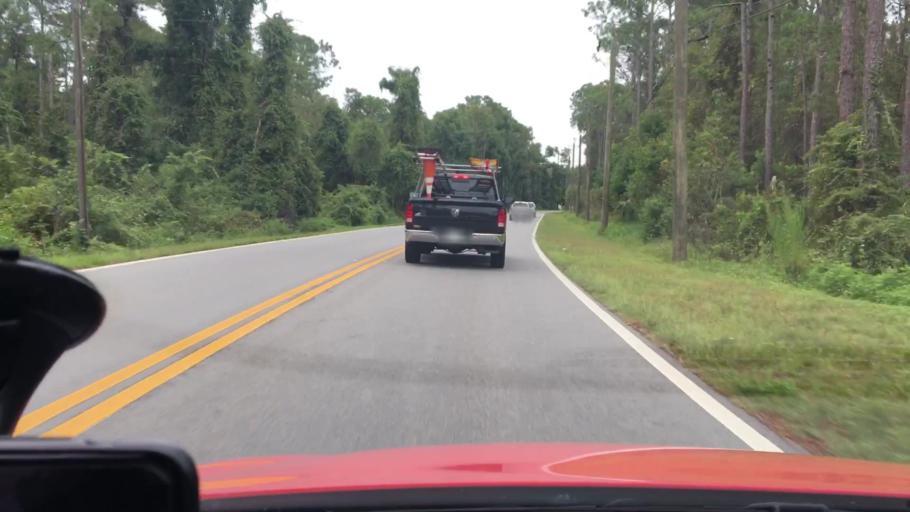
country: US
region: Florida
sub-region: Flagler County
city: Flagler Beach
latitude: 29.5084
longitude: -81.1924
